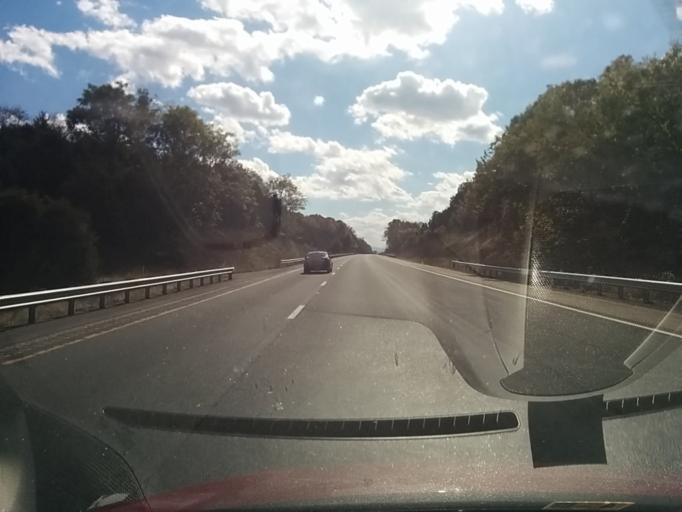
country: US
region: Virginia
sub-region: Rockbridge County
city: East Lexington
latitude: 37.8369
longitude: -79.3695
